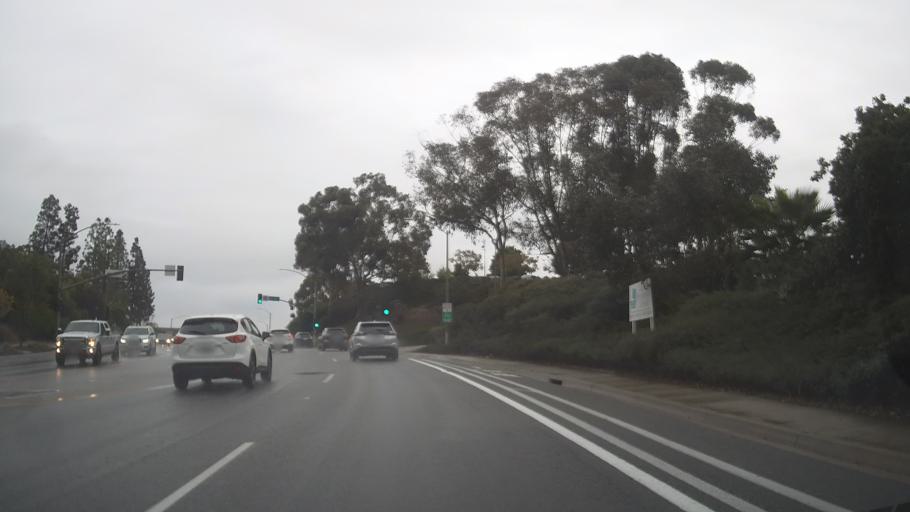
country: US
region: California
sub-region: San Diego County
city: Encinitas
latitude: 33.0452
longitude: -117.2693
